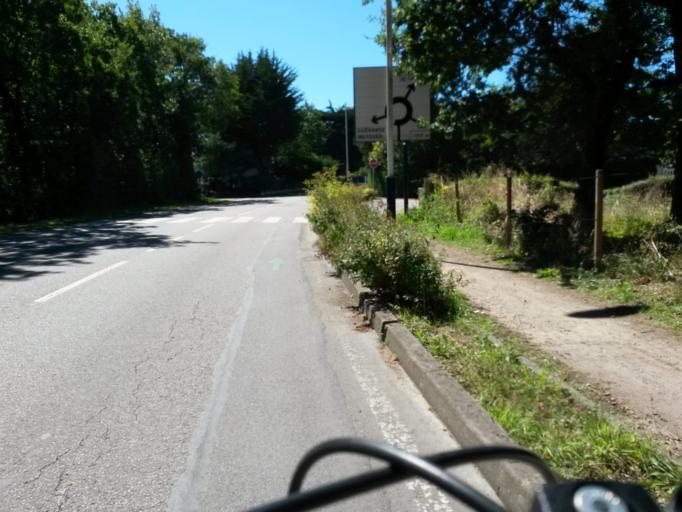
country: FR
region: Pays de la Loire
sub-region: Departement de la Loire-Atlantique
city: Mesquer
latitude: 47.4020
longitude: -2.4881
